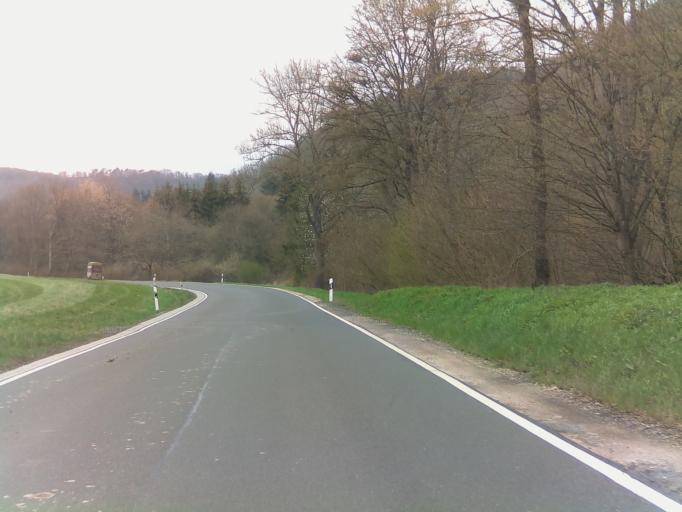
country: DE
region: Rheinland-Pfalz
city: Heinzenberg
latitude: 49.8281
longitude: 7.4888
